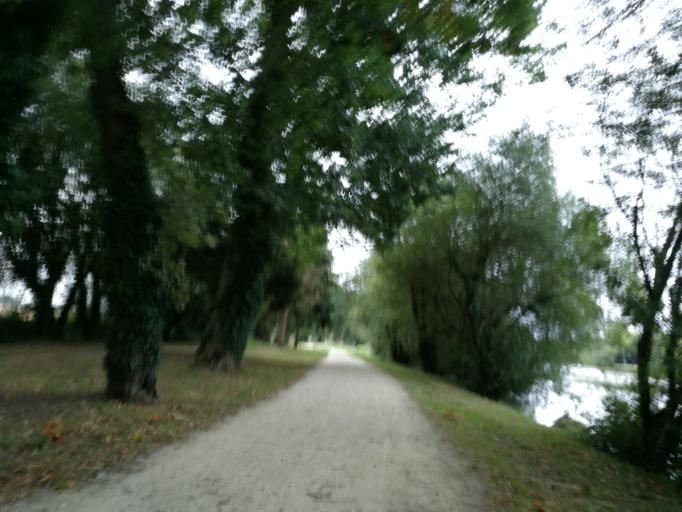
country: FR
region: Brittany
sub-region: Departement d'Ille-et-Vilaine
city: Bedee
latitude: 48.1689
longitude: -1.9532
